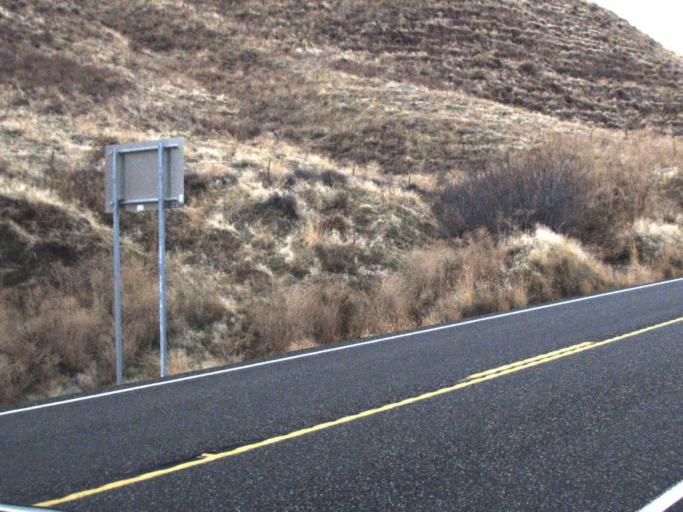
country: US
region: Washington
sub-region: Garfield County
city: Pomeroy
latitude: 46.4366
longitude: -117.3521
